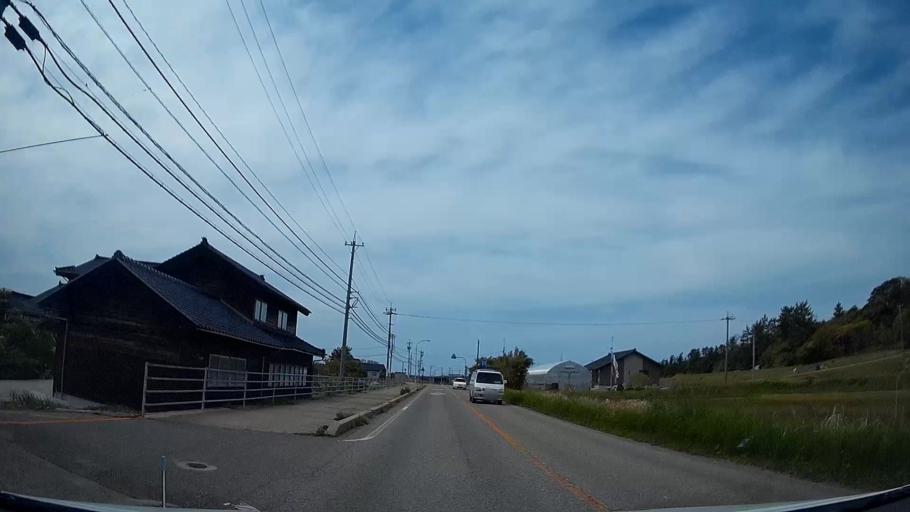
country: JP
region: Ishikawa
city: Hakui
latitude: 37.0378
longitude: 136.7438
